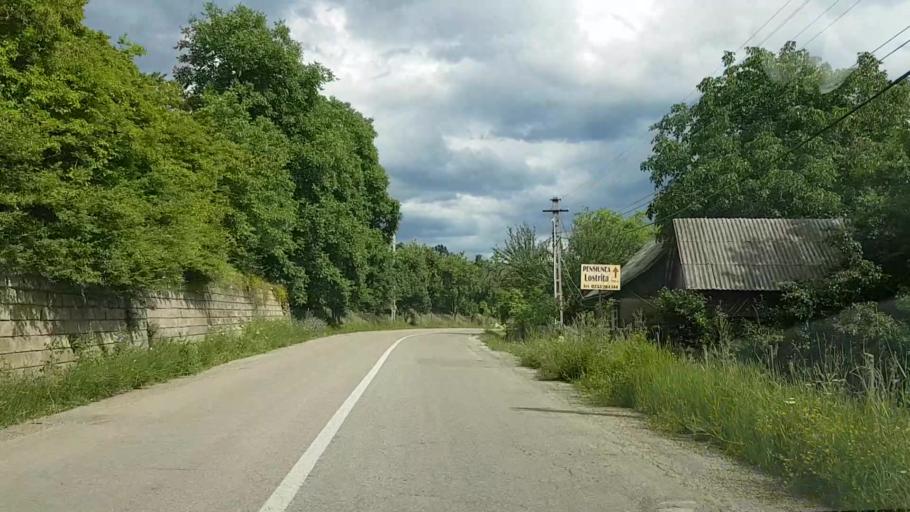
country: RO
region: Neamt
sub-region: Comuna Hangu
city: Hangu
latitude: 47.0258
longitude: 26.0679
